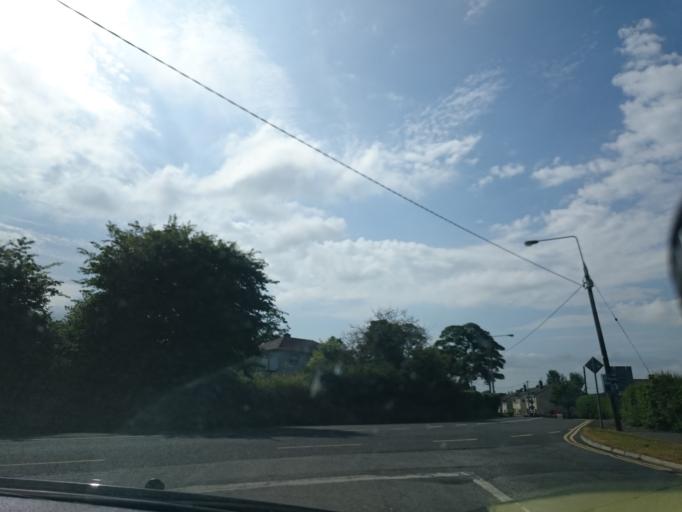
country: IE
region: Leinster
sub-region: Kilkenny
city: Thomastown
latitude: 52.5344
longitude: -7.2229
